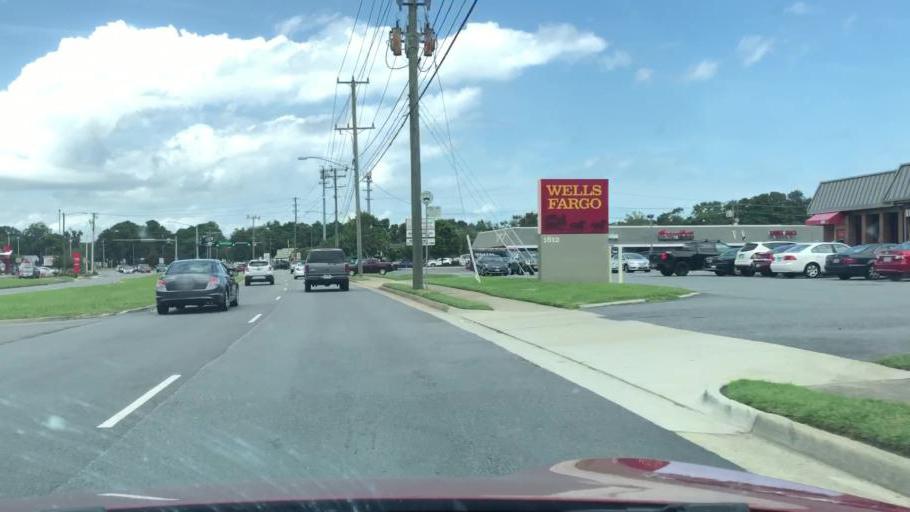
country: US
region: Virginia
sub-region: City of Norfolk
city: Norfolk
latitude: 36.8931
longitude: -76.1405
